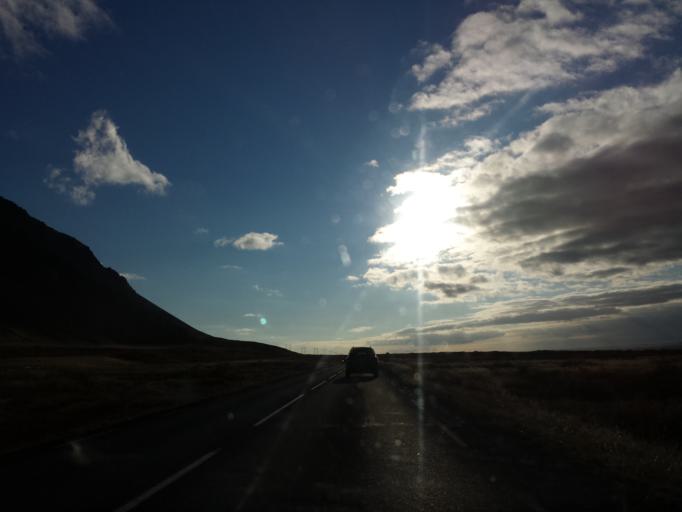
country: IS
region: West
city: Borgarnes
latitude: 64.5069
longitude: -21.9219
